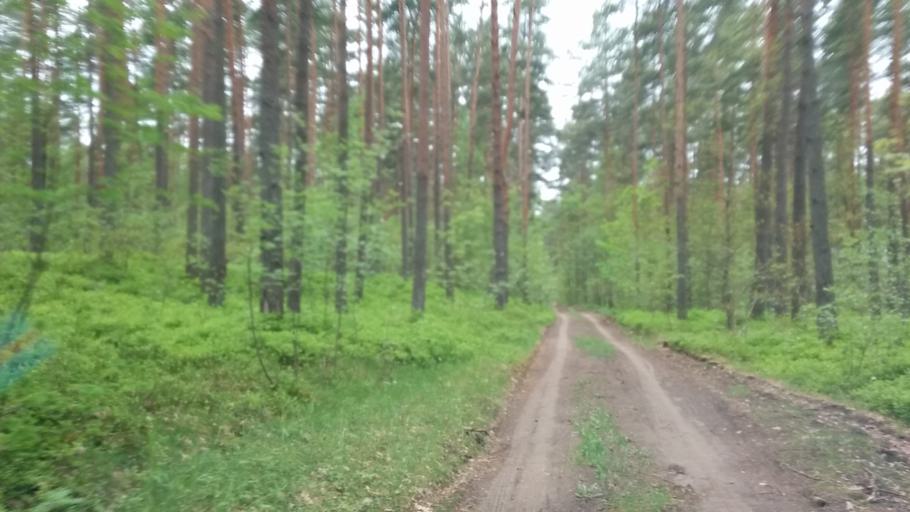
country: LV
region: Babite
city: Pinki
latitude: 56.9405
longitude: 23.9285
